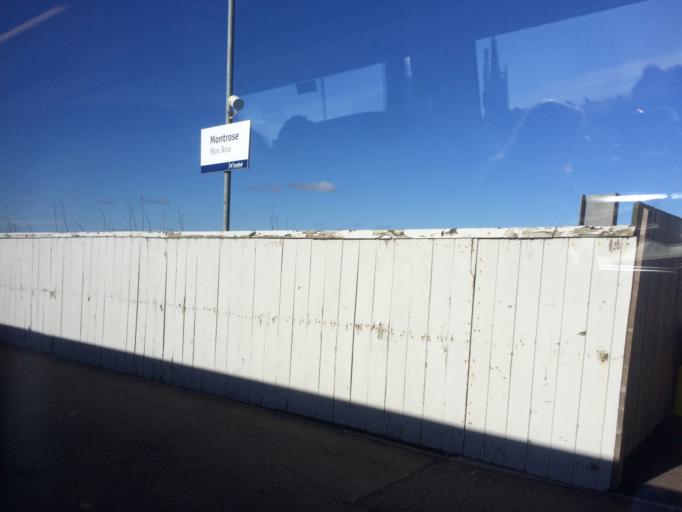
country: GB
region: Scotland
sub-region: Angus
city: Montrose
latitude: 56.7122
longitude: -2.4726
